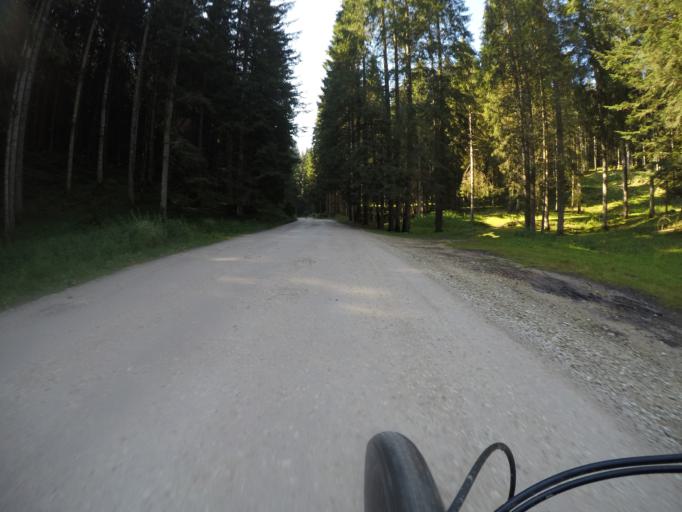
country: IT
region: Veneto
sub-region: Provincia di Vicenza
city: Asiago
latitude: 45.8497
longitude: 11.5266
